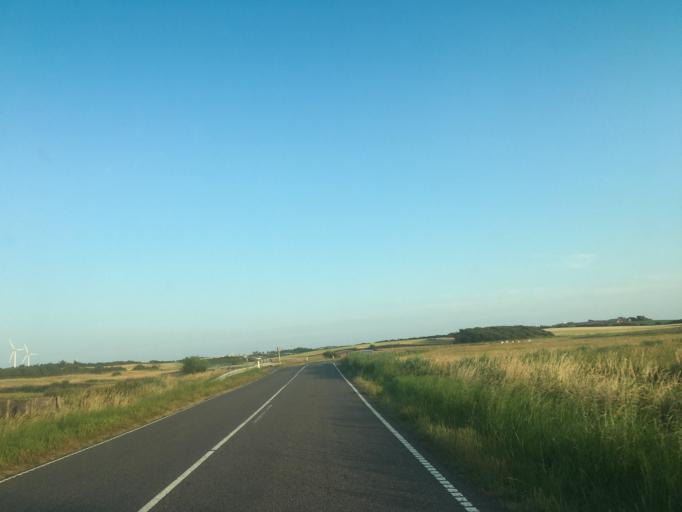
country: DK
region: North Denmark
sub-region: Thisted Kommune
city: Hurup
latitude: 56.8146
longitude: 8.3480
